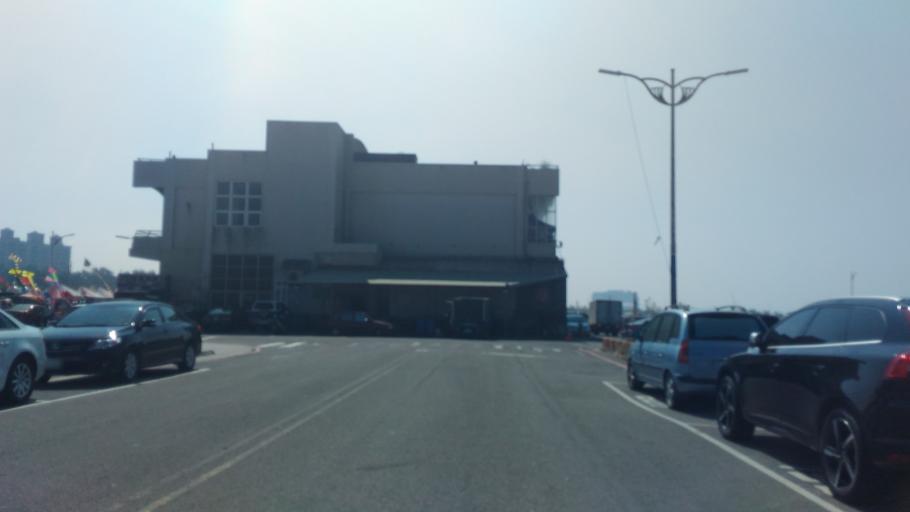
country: TW
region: Taiwan
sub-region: Hsinchu
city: Hsinchu
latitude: 24.8492
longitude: 120.9253
